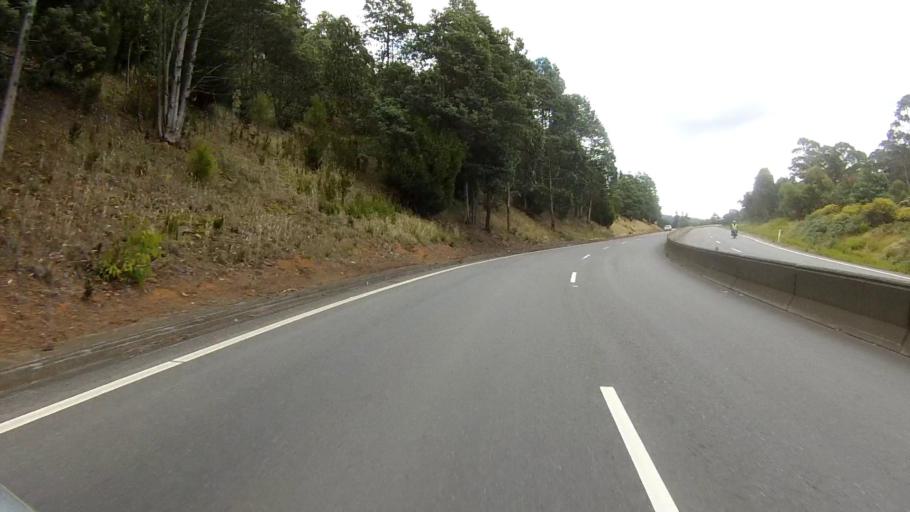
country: AU
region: Tasmania
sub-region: Kingborough
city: Margate
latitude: -42.9812
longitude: 147.1731
